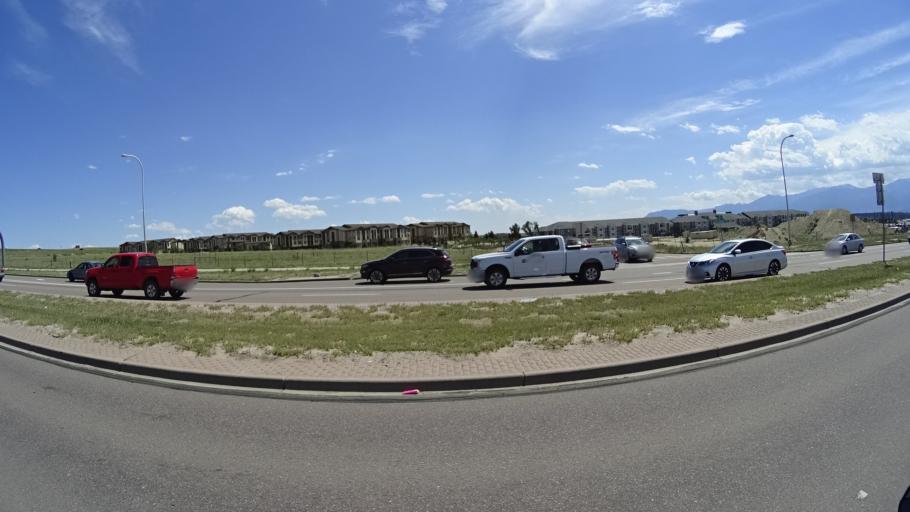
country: US
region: Colorado
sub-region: El Paso County
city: Black Forest
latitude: 38.9404
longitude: -104.7244
